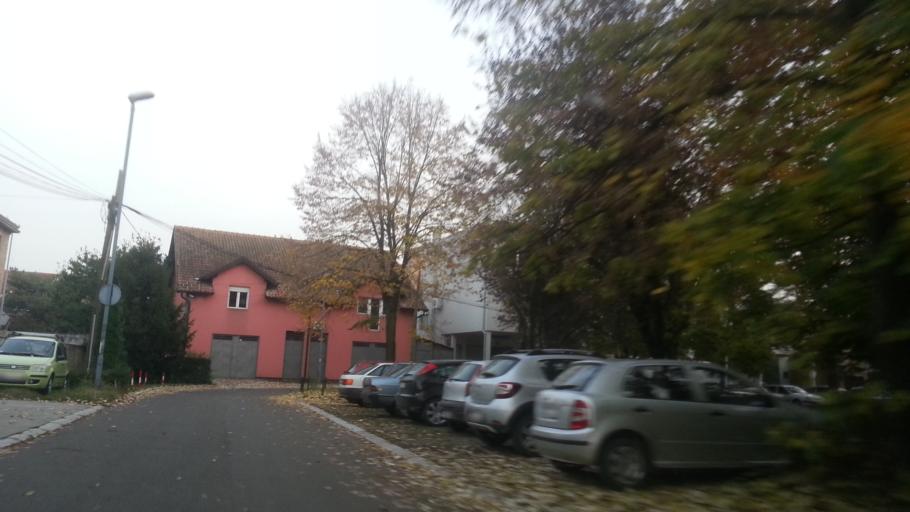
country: RS
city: Novi Banovci
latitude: 44.8950
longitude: 20.2949
